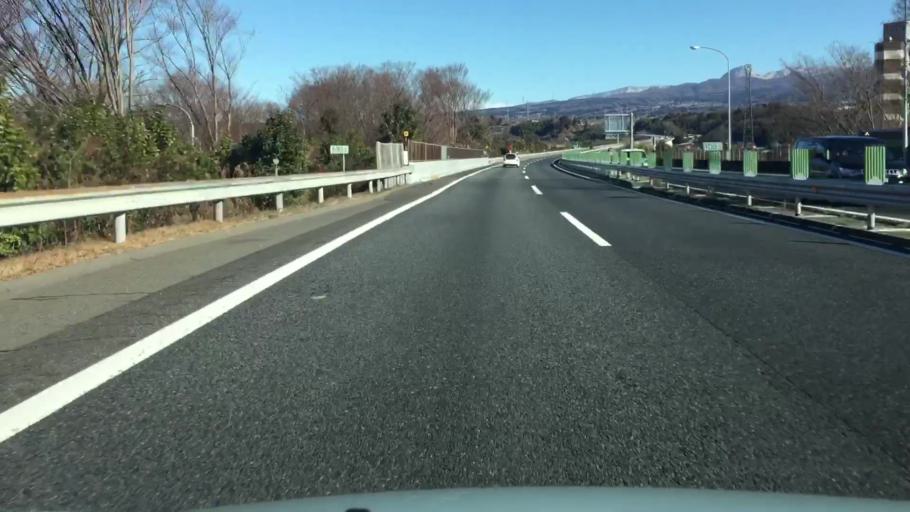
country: JP
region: Gunma
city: Shibukawa
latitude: 36.4777
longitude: 139.0174
